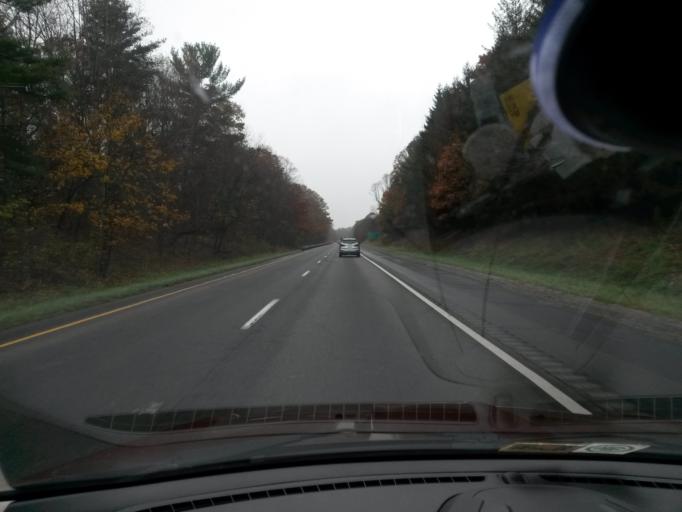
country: US
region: Virginia
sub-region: Carroll County
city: Hillsville
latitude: 36.7552
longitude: -80.7819
